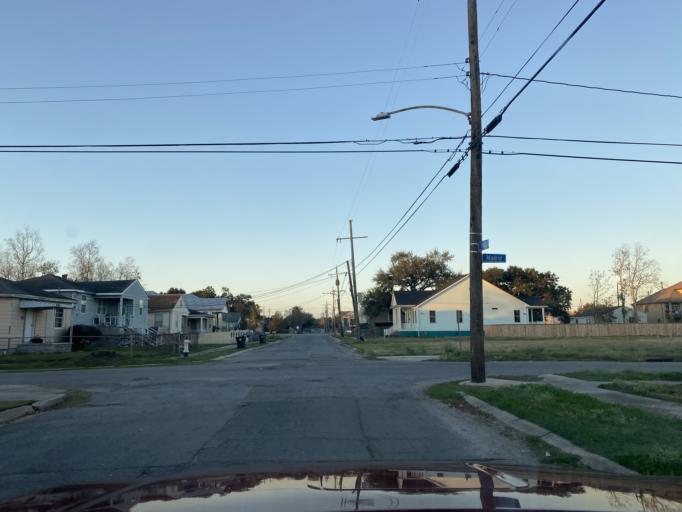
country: US
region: Louisiana
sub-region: Orleans Parish
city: New Orleans
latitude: 30.0211
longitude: -90.0551
